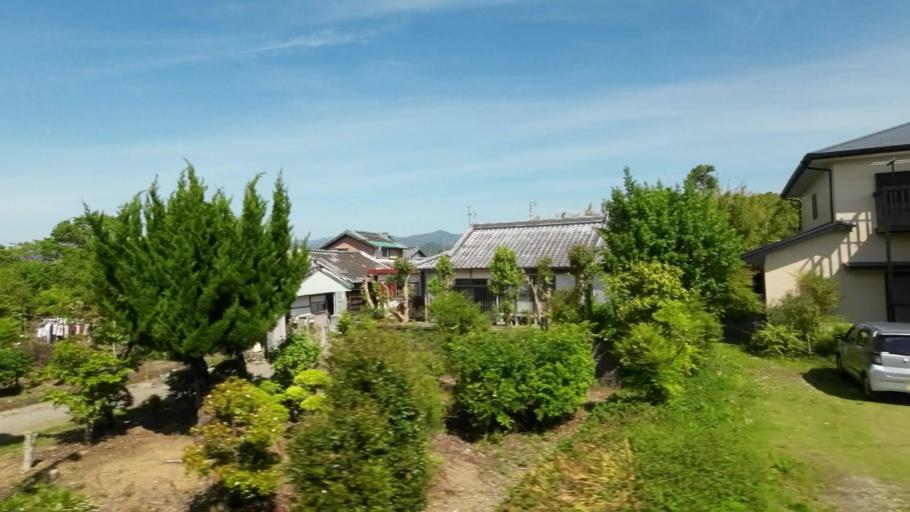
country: JP
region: Kochi
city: Kochi-shi
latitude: 33.5897
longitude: 133.6599
